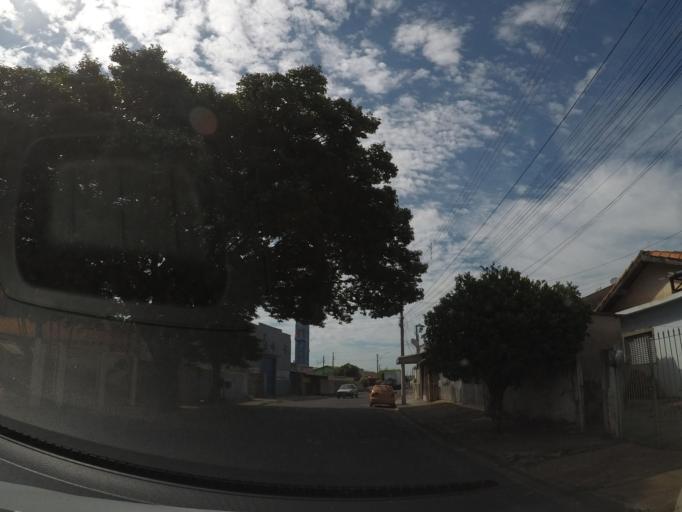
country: BR
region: Sao Paulo
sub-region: Hortolandia
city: Hortolandia
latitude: -22.8334
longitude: -47.1832
